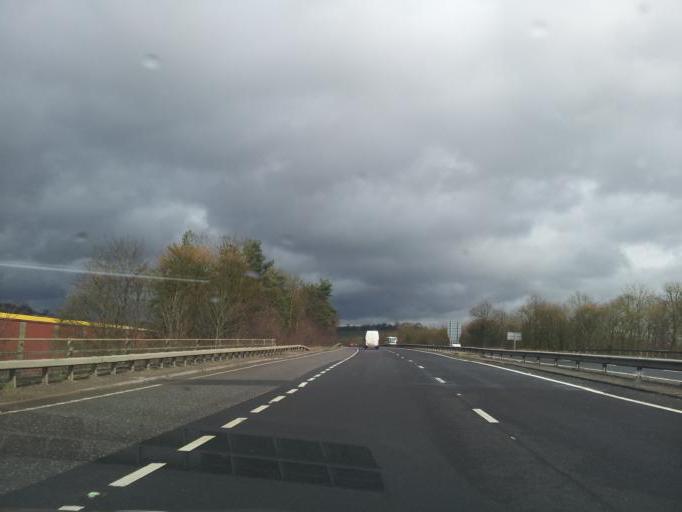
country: GB
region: England
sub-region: Somerset
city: Wincanton
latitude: 51.0490
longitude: -2.4129
